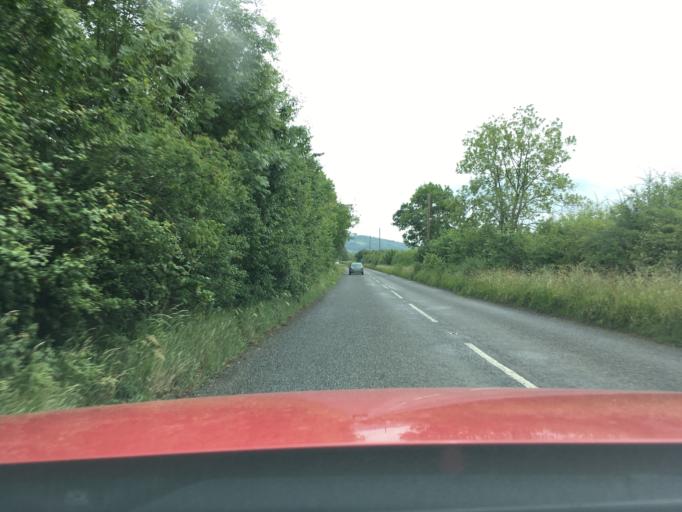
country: GB
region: England
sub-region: Gloucestershire
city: Winchcombe
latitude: 51.9995
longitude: -1.9649
